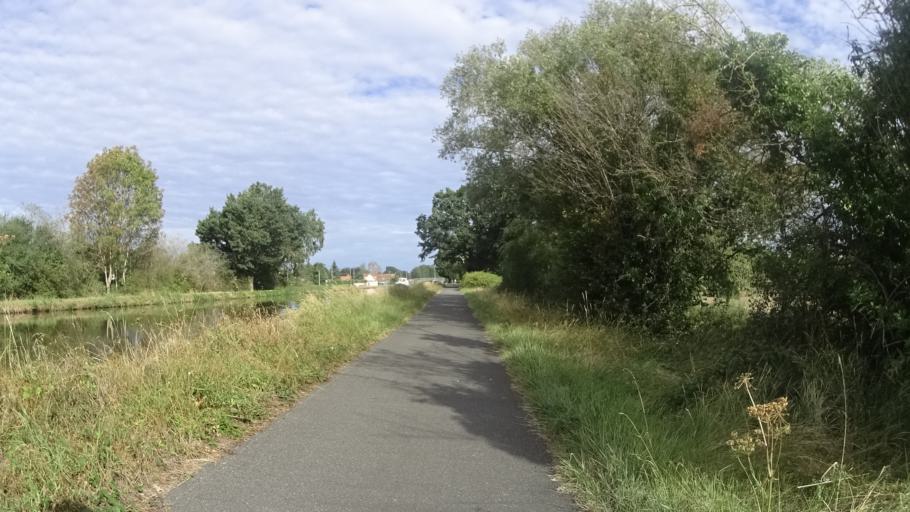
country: FR
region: Auvergne
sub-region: Departement de l'Allier
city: Diou
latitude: 46.5234
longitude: 3.7776
